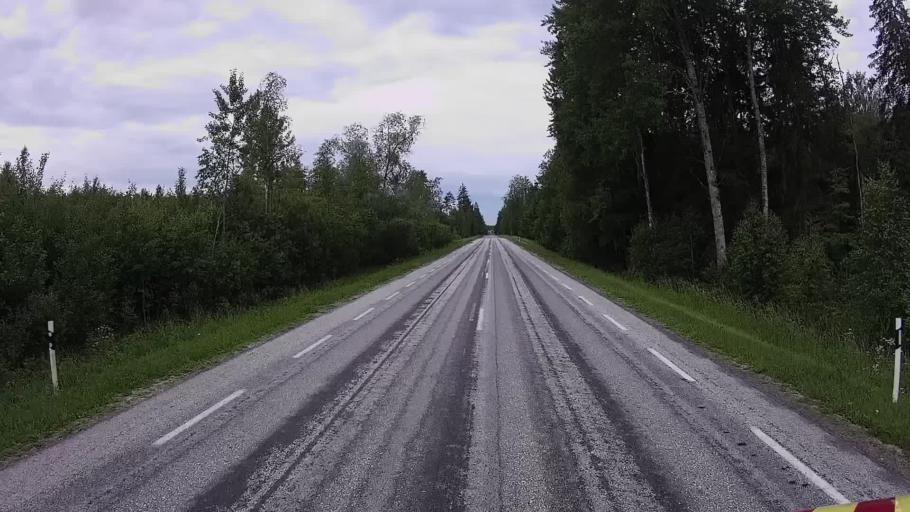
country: EE
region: Viljandimaa
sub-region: Karksi vald
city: Karksi-Nuia
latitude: 58.1922
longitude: 25.6076
